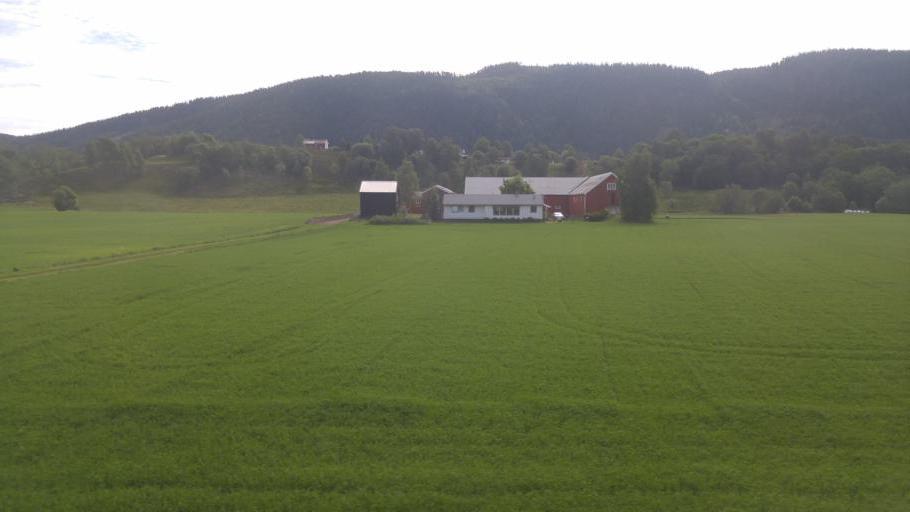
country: NO
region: Sor-Trondelag
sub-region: Melhus
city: Lundamo
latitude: 63.1690
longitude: 10.3007
